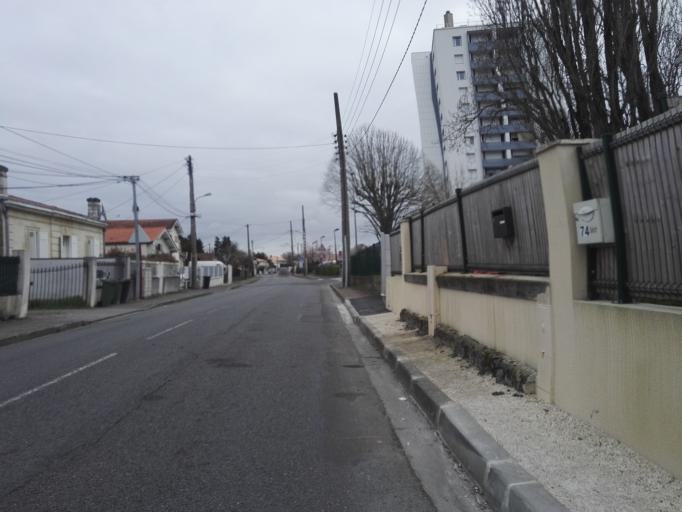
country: FR
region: Aquitaine
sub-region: Departement de la Gironde
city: Talence
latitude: 44.7827
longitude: -0.5763
